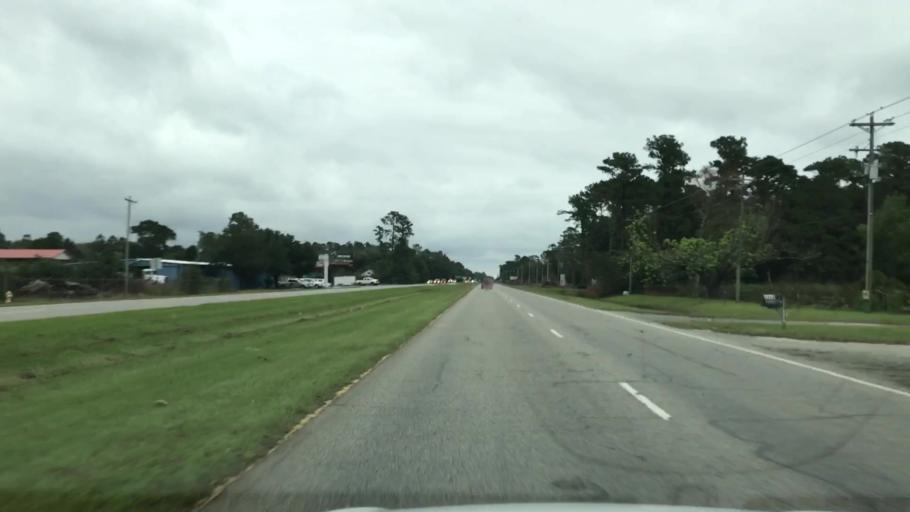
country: US
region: South Carolina
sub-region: Georgetown County
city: Georgetown
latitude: 33.3158
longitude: -79.3266
